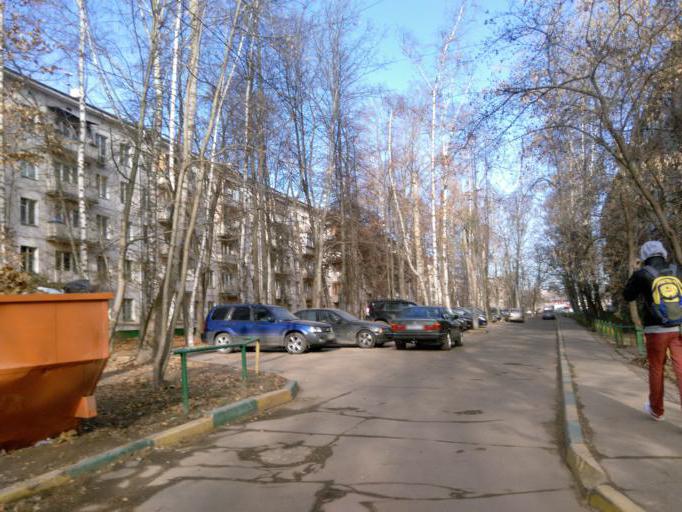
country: RU
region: Moscow
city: Troparevo
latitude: 55.6706
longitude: 37.5074
